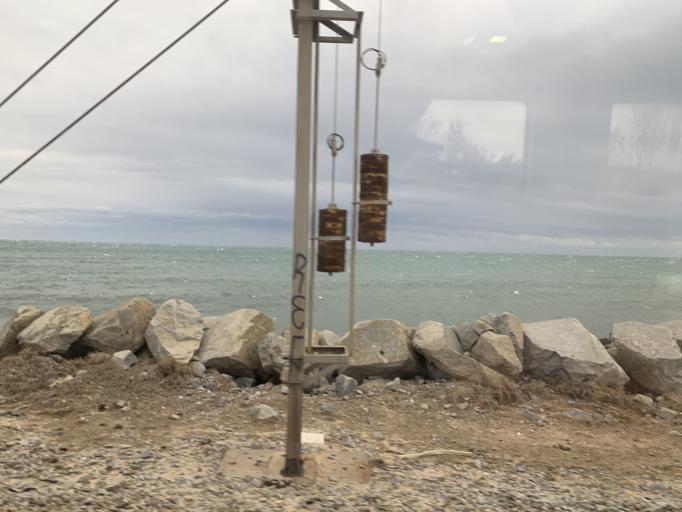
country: ES
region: Catalonia
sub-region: Provincia de Barcelona
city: Mataro
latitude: 41.5260
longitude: 2.4350
